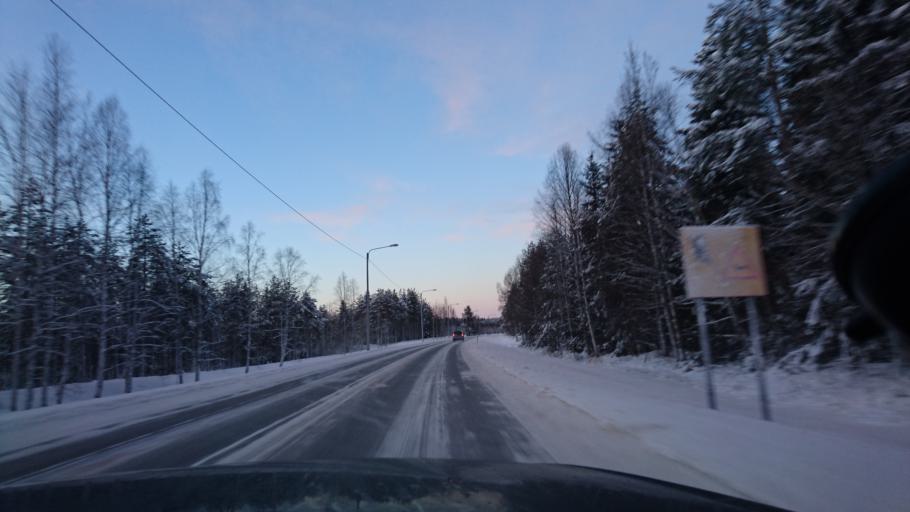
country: FI
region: Lapland
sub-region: Rovaniemi
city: Ranua
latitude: 65.9338
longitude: 26.4975
